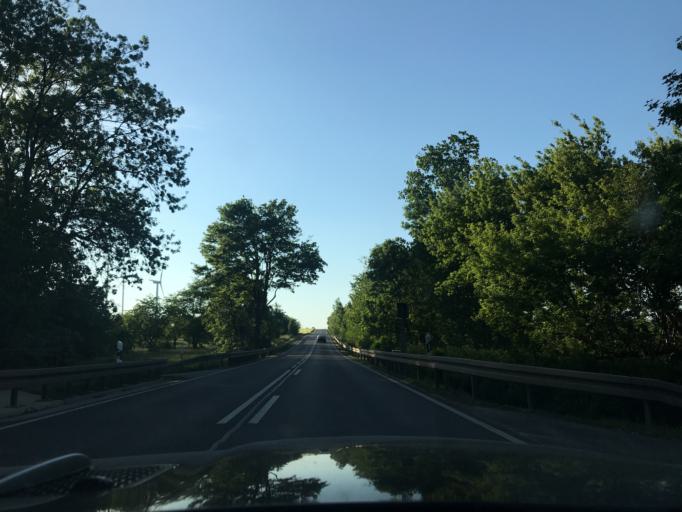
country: DE
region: Thuringia
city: Hochheim
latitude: 51.0332
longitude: 10.6703
